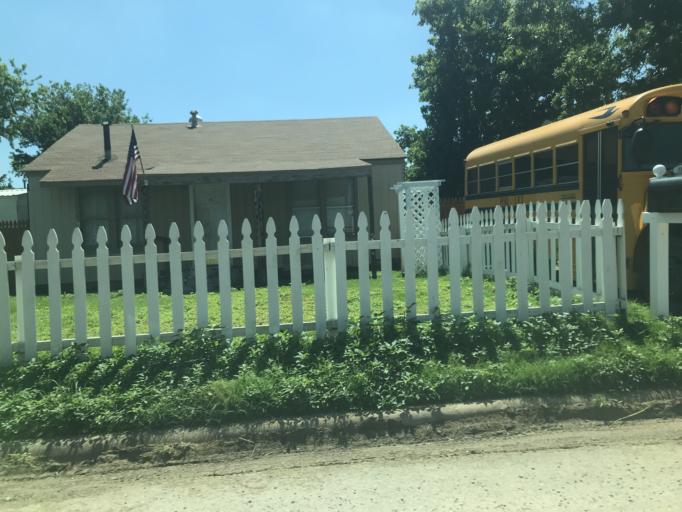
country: US
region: Texas
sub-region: Taylor County
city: Abilene
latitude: 32.4708
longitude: -99.7431
